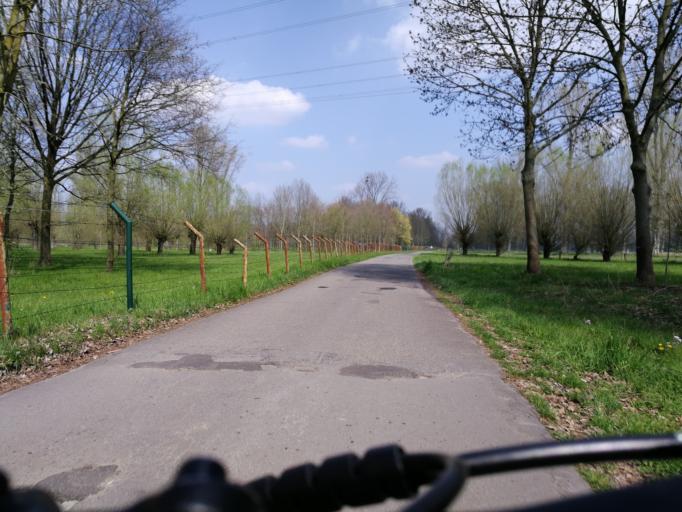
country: DE
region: North Rhine-Westphalia
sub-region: Regierungsbezirk Dusseldorf
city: Dormagen
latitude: 51.1518
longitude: 6.8344
